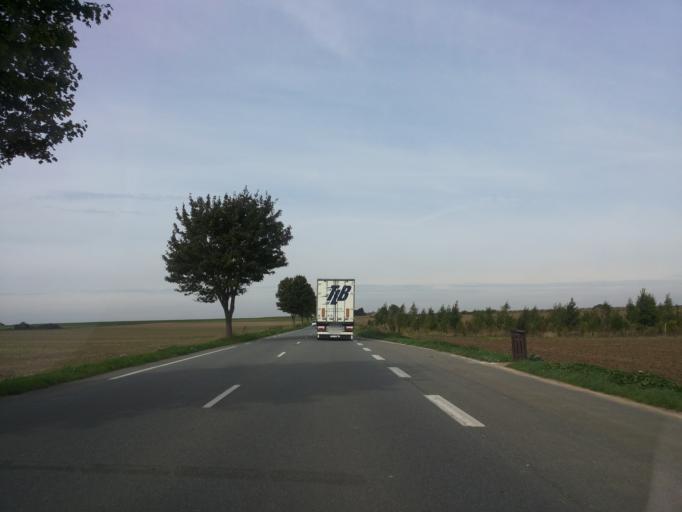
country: FR
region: Nord-Pas-de-Calais
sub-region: Departement du Pas-de-Calais
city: Biache-Saint-Vaast
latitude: 50.2411
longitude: 2.9679
